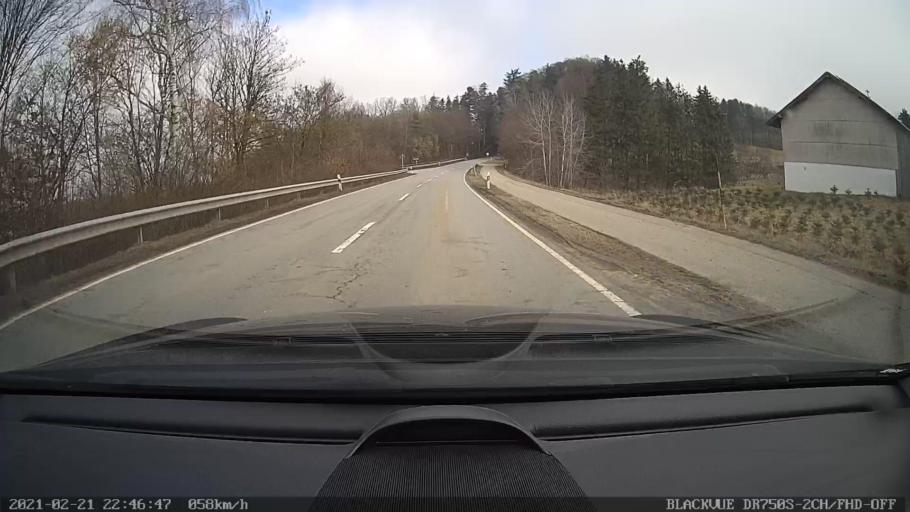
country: DE
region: Bavaria
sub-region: Upper Bavaria
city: Griesstatt
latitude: 48.0096
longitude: 12.1873
